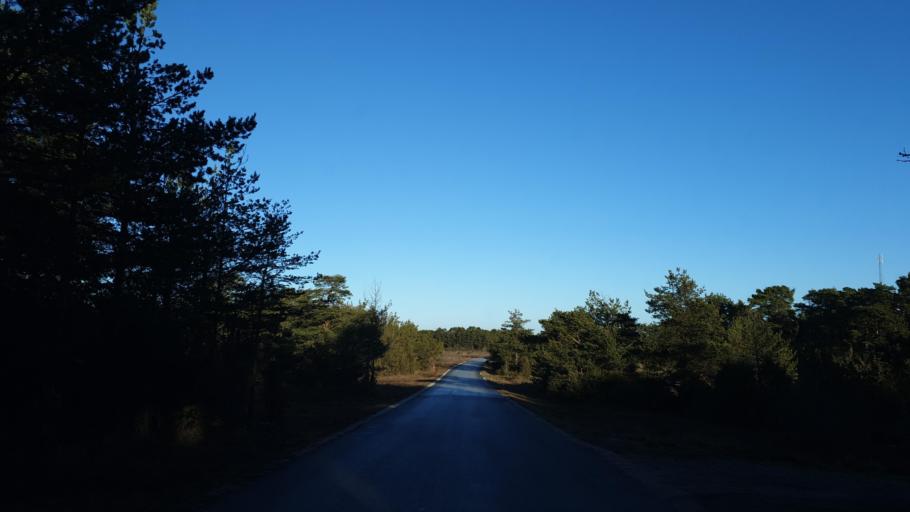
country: SE
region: Gotland
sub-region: Gotland
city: Slite
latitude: 57.9396
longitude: 19.1503
